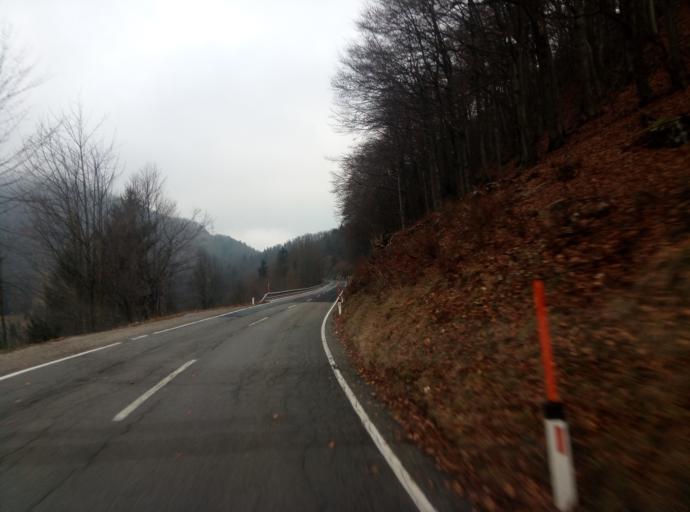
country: SI
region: Idrija
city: Idrija
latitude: 45.9160
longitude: 14.0330
